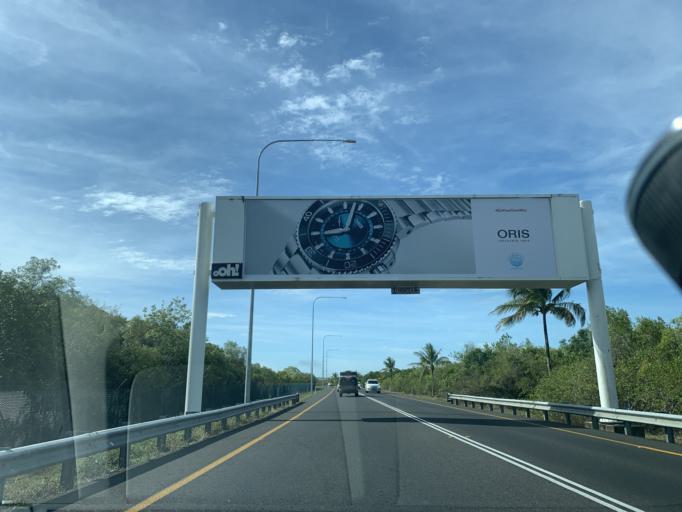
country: AU
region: Queensland
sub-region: Cairns
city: Cairns
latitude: -16.8835
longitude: 145.7609
